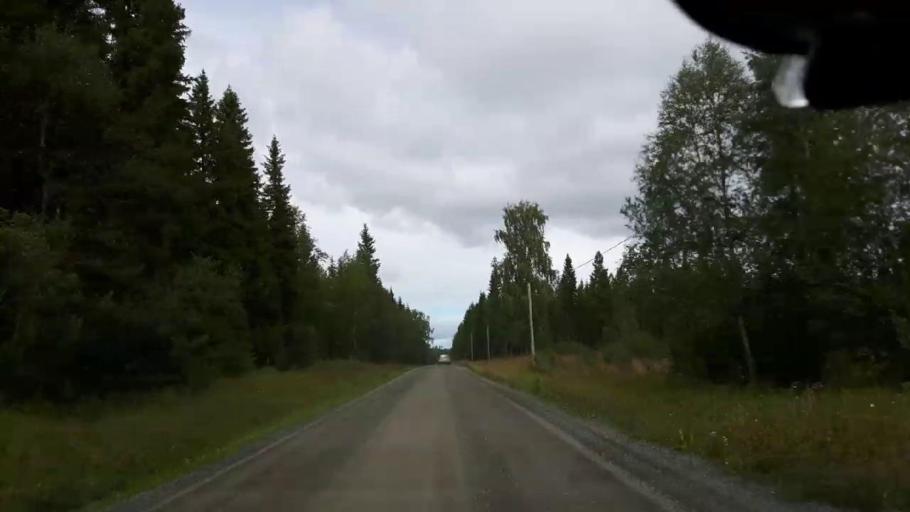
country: SE
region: Jaemtland
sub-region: Krokoms Kommun
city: Valla
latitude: 63.3972
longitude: 14.0994
